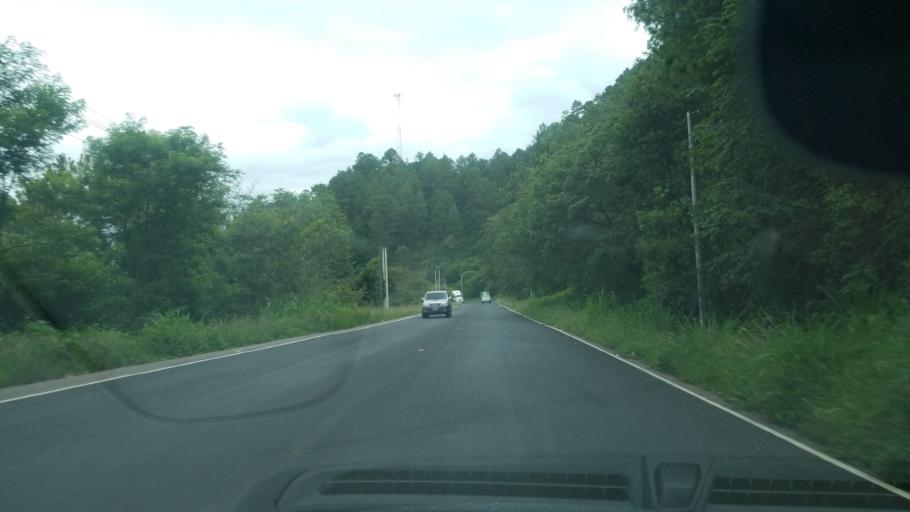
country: HN
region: Ocotepeque
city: Sinuapa
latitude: 14.4552
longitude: -89.1436
